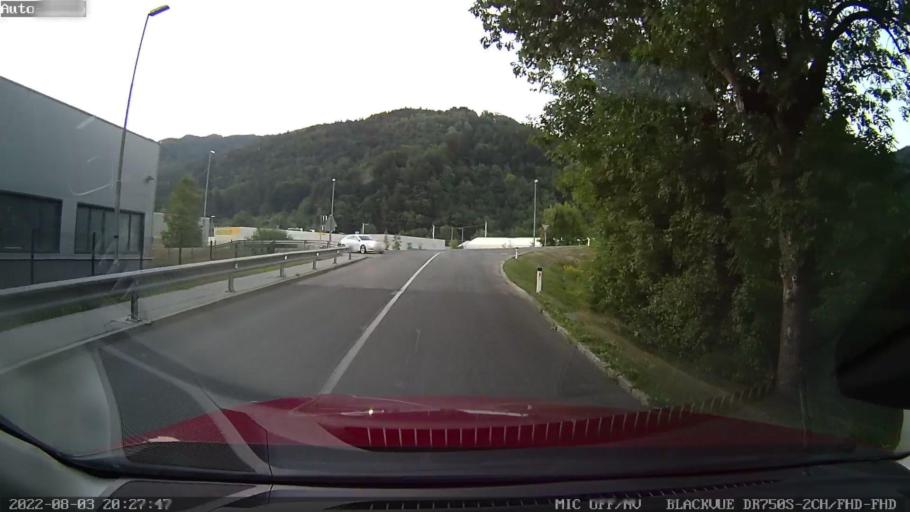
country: SI
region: Jesenice
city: Hrusica
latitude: 46.4400
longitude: 14.0343
